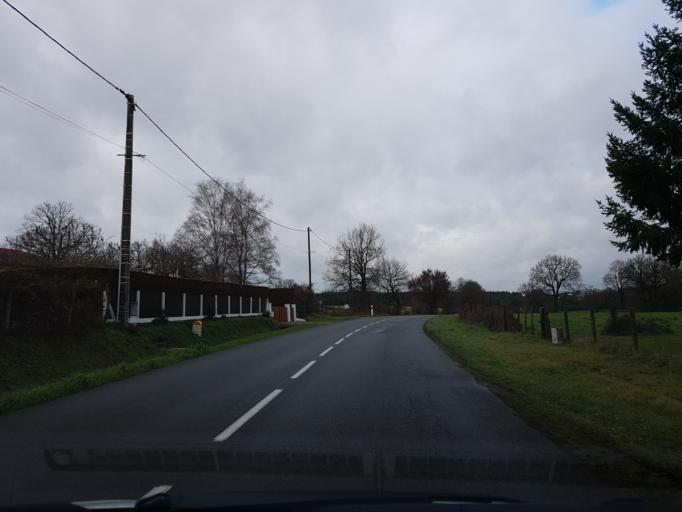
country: FR
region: Poitou-Charentes
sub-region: Departement de la Charente
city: Chabanais
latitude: 45.8979
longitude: 0.7307
